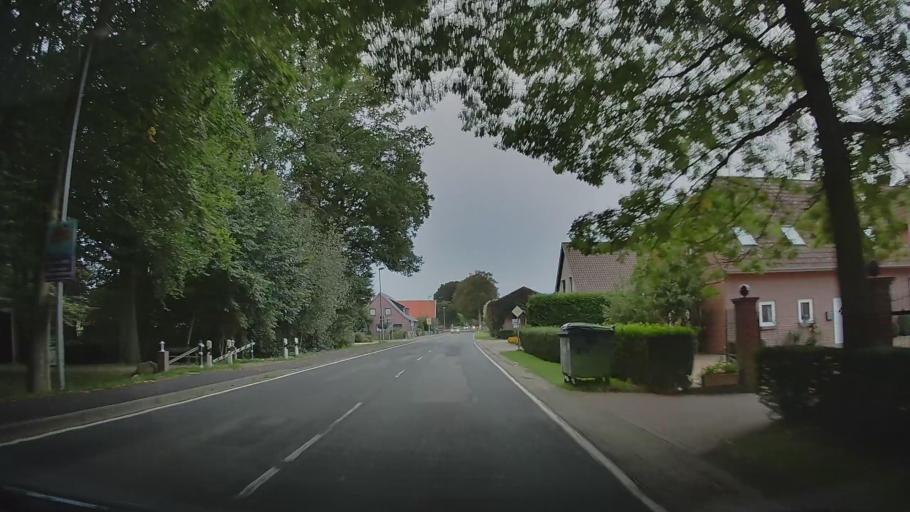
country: DE
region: Lower Saxony
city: Syke
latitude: 52.9056
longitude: 8.8762
